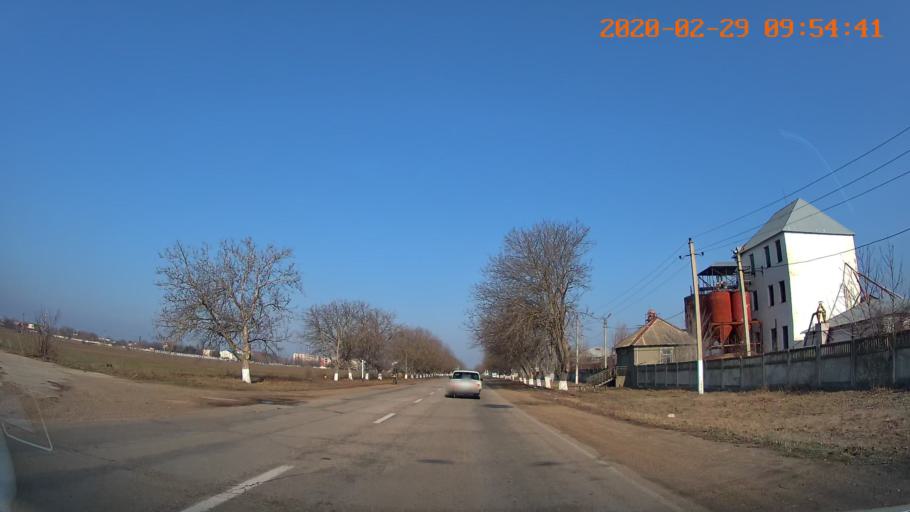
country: MD
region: Telenesti
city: Slobozia
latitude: 46.7303
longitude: 29.7143
